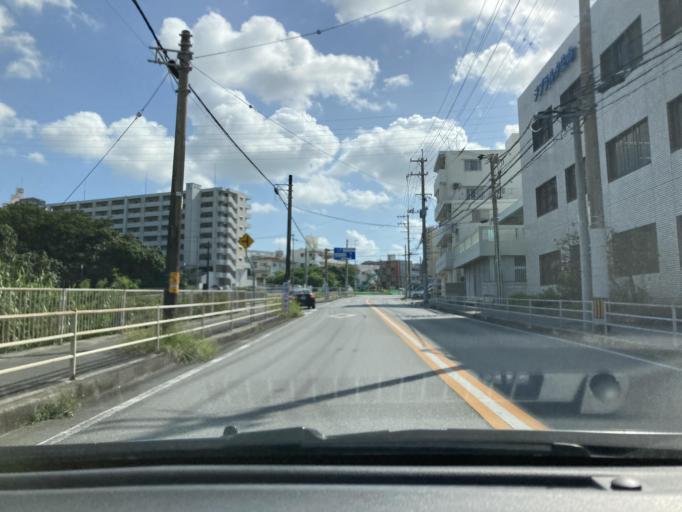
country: JP
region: Okinawa
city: Tomigusuku
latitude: 26.1890
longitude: 127.6808
